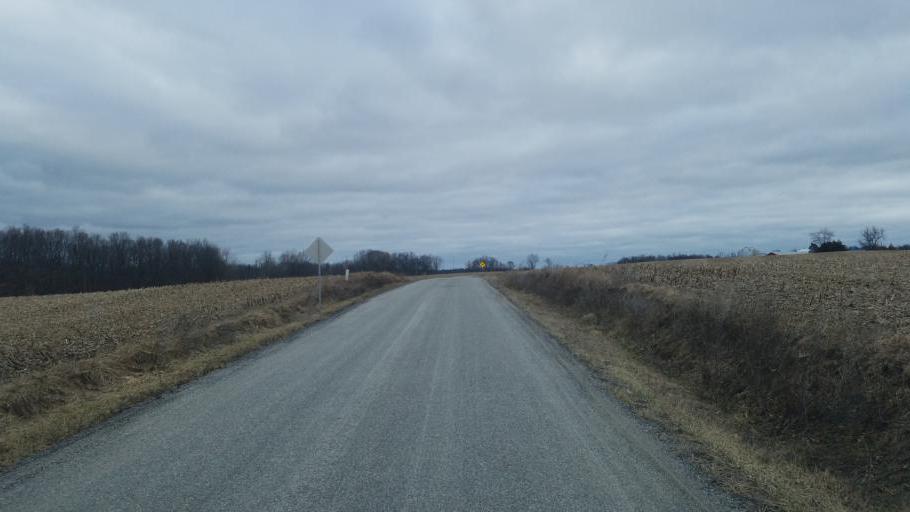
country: US
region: Ohio
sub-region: Morrow County
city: Mount Gilead
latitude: 40.5757
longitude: -82.6965
